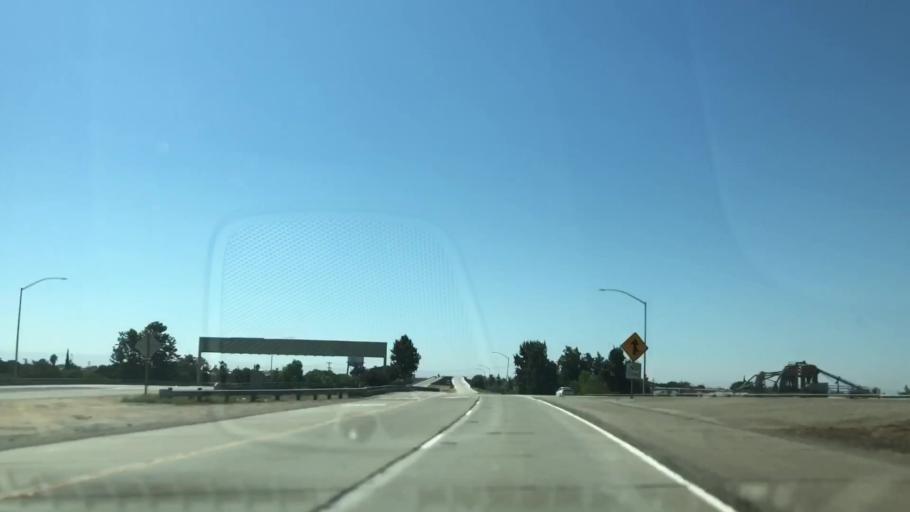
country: US
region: California
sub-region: San Joaquin County
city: Stockton
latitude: 37.9467
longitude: -121.3061
